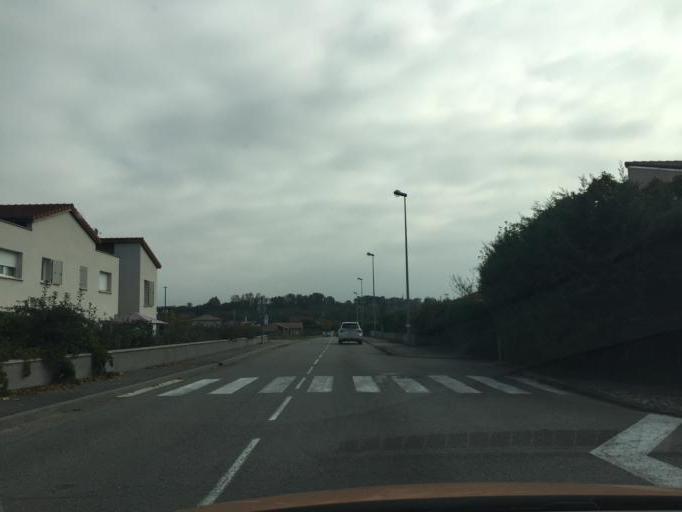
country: FR
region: Rhone-Alpes
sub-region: Departement de la Drome
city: Portes-les-Valence
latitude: 44.8803
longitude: 4.8826
